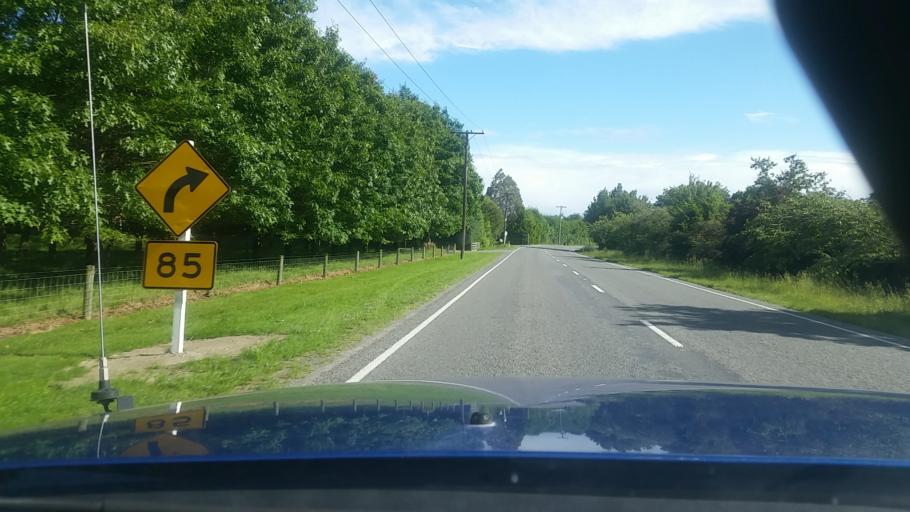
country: NZ
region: Canterbury
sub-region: Ashburton District
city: Ashburton
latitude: -43.8695
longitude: 171.7273
